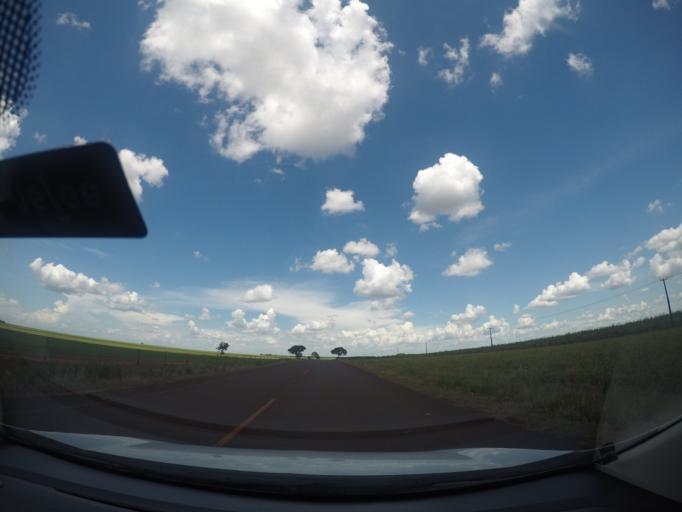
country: BR
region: Minas Gerais
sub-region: Frutal
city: Frutal
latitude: -19.9219
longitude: -48.6758
